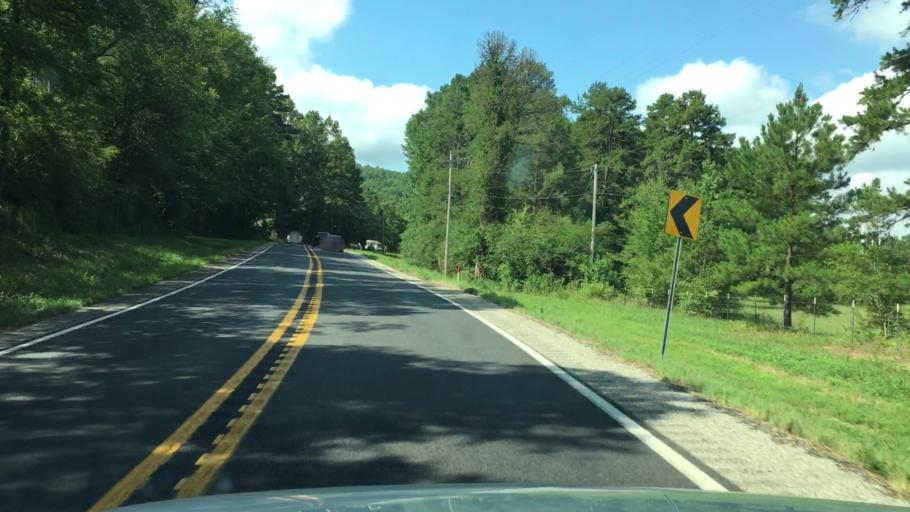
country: US
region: Arkansas
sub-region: Garland County
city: Lake Hamilton
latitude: 34.3825
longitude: -93.1342
